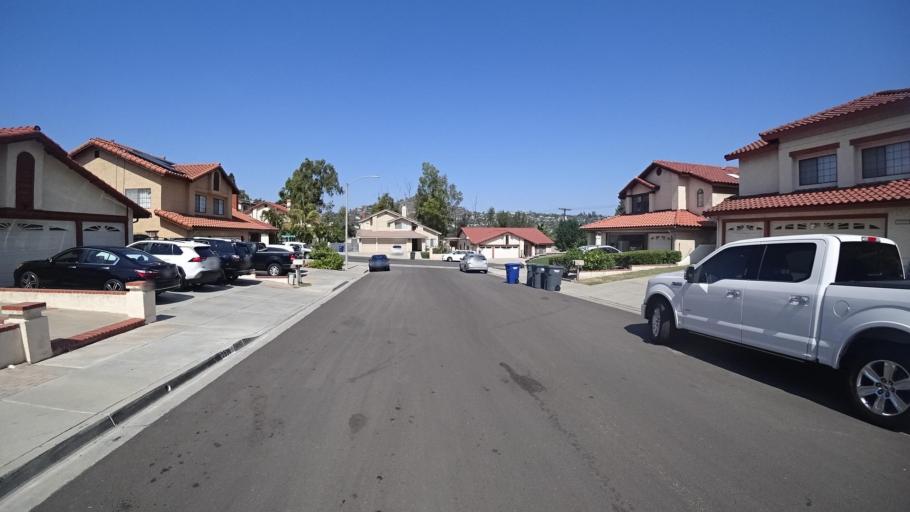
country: US
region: California
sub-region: San Diego County
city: Spring Valley
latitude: 32.7440
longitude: -116.9890
